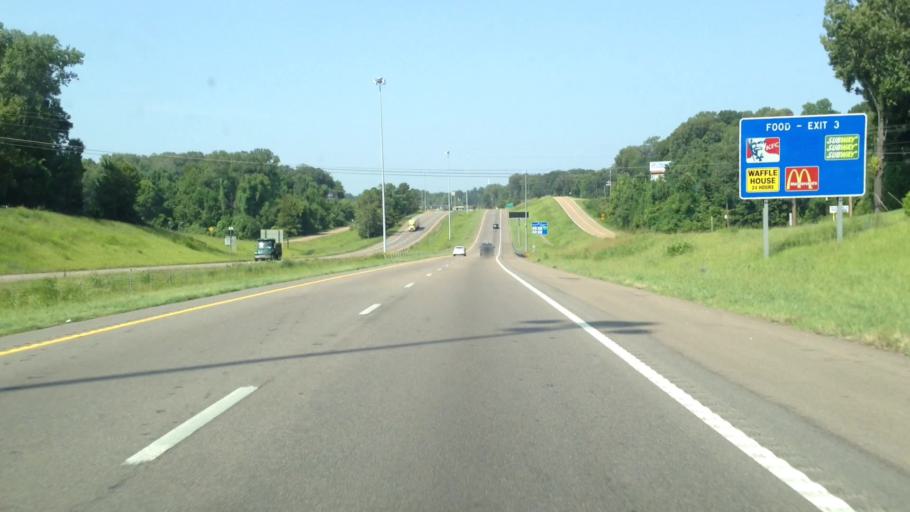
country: US
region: Mississippi
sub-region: Warren County
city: Beechwood
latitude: 32.3366
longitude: -90.8534
